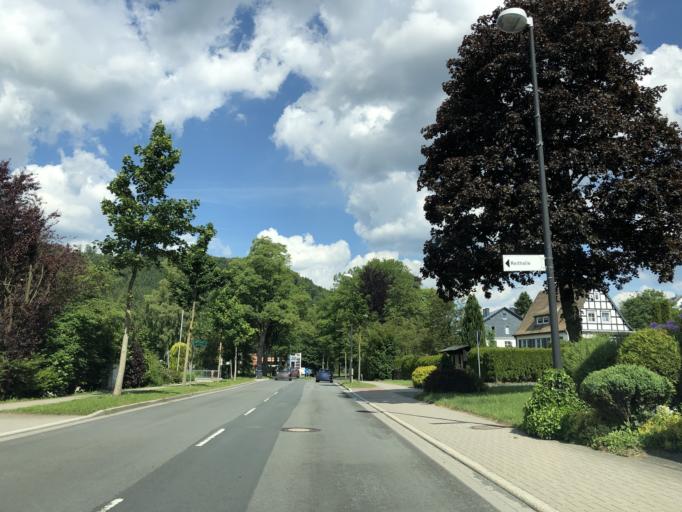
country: DE
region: North Rhine-Westphalia
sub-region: Regierungsbezirk Arnsberg
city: Winterberg
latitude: 51.2622
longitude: 8.5268
